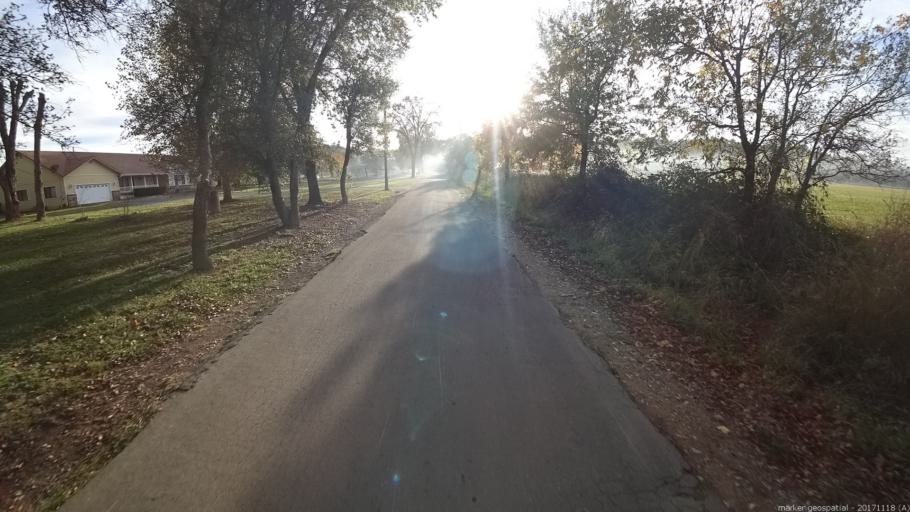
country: US
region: California
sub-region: Shasta County
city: Anderson
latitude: 40.4539
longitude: -122.3218
